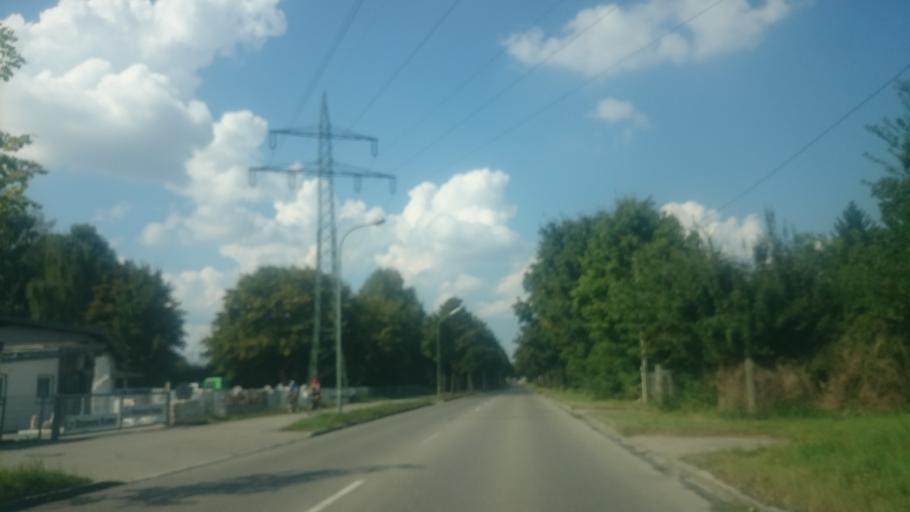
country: DE
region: Bavaria
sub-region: Swabia
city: Friedberg
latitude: 48.3678
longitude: 10.9441
